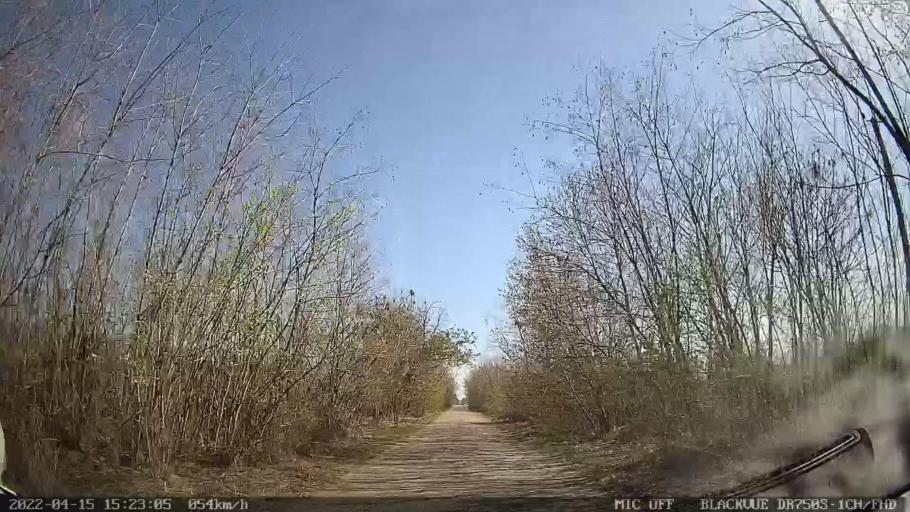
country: MD
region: Raionul Ocnita
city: Otaci
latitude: 48.3771
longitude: 27.9178
